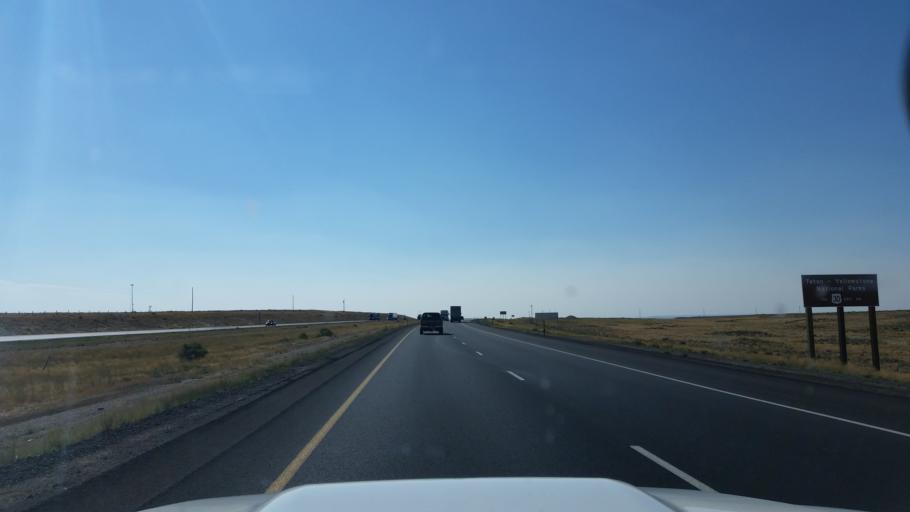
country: US
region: Wyoming
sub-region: Sweetwater County
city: Green River
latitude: 41.5419
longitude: -109.8884
